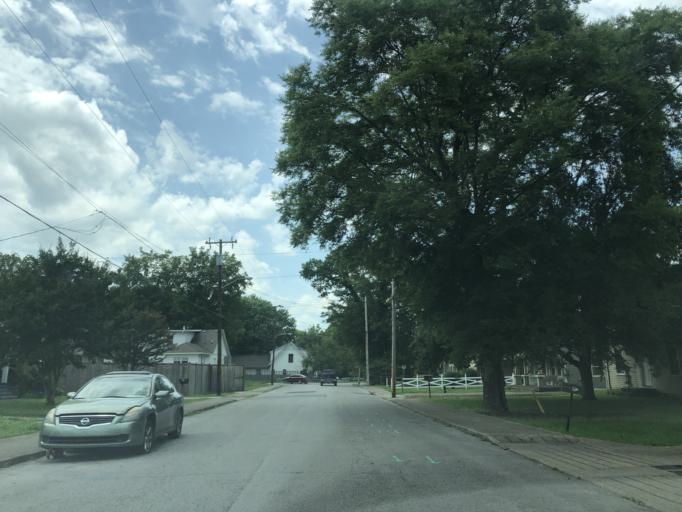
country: US
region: Tennessee
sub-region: Davidson County
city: Nashville
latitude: 36.1872
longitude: -86.7530
